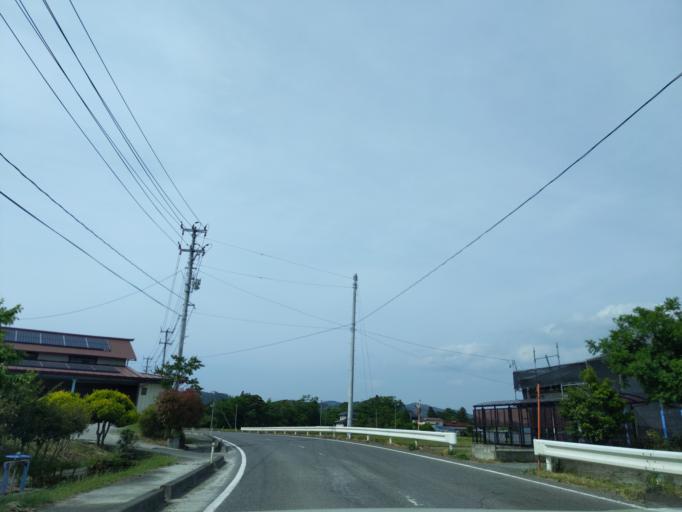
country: JP
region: Fukushima
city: Koriyama
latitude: 37.4632
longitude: 140.3136
